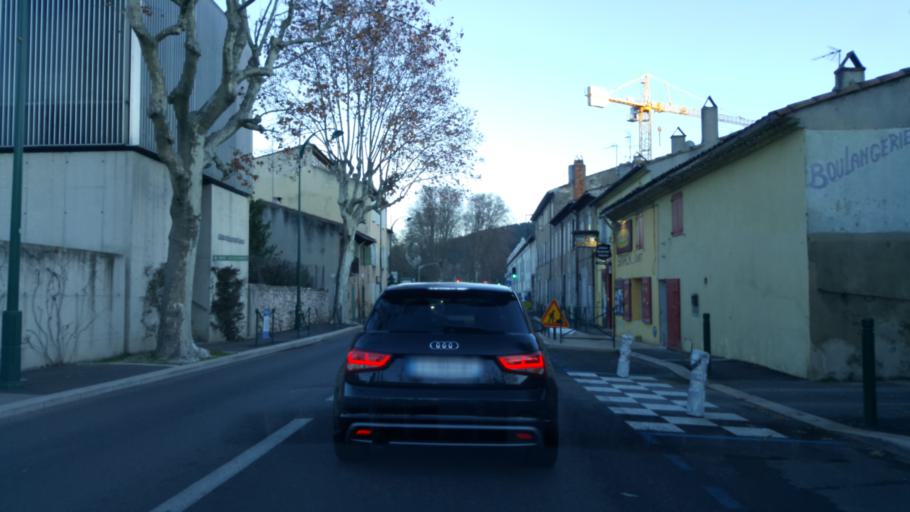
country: FR
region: Provence-Alpes-Cote d'Azur
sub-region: Departement des Bouches-du-Rhone
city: Meyreuil
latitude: 43.5094
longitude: 5.4906
